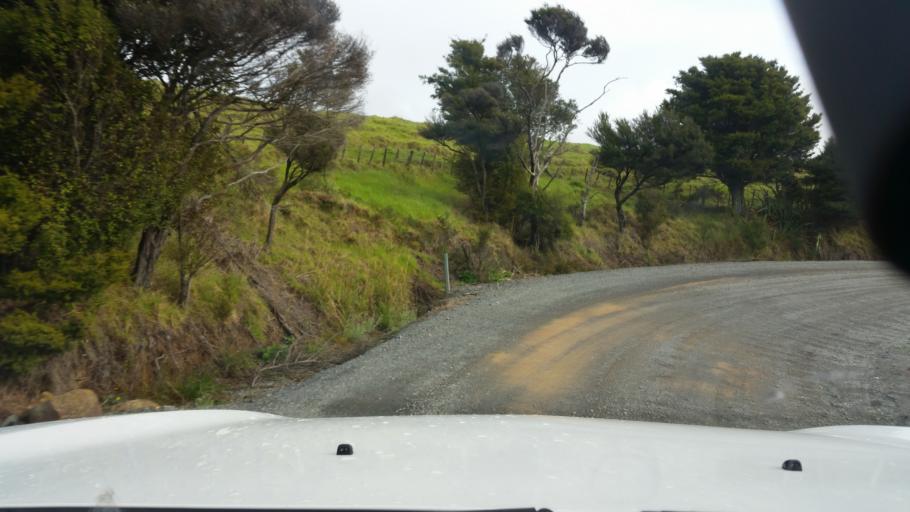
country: NZ
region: Northland
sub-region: Whangarei
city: Ngunguru
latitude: -35.7678
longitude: 174.5303
